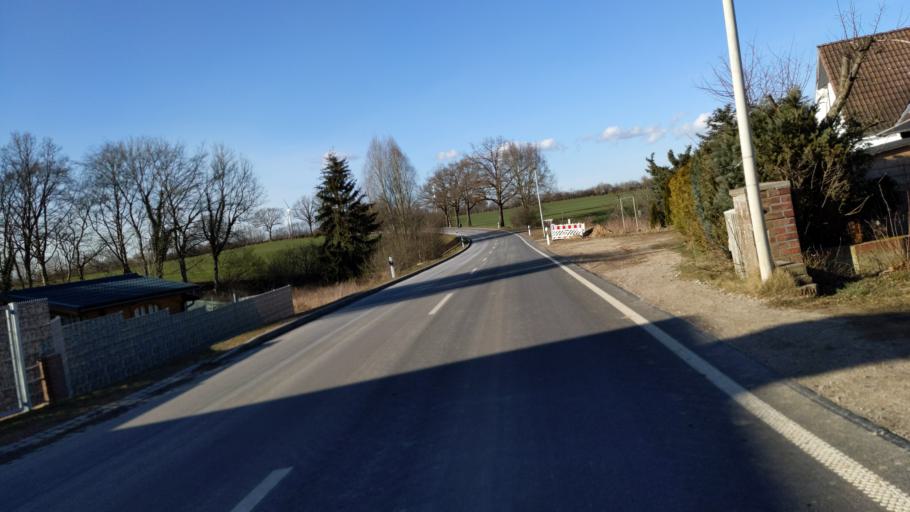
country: DE
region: Schleswig-Holstein
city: Susel
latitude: 54.0473
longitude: 10.6583
